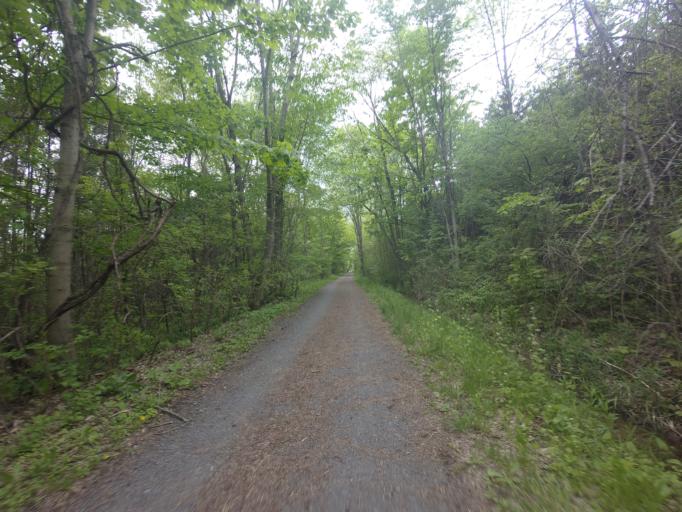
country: CA
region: Ontario
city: Kingston
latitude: 44.3008
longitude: -76.5692
